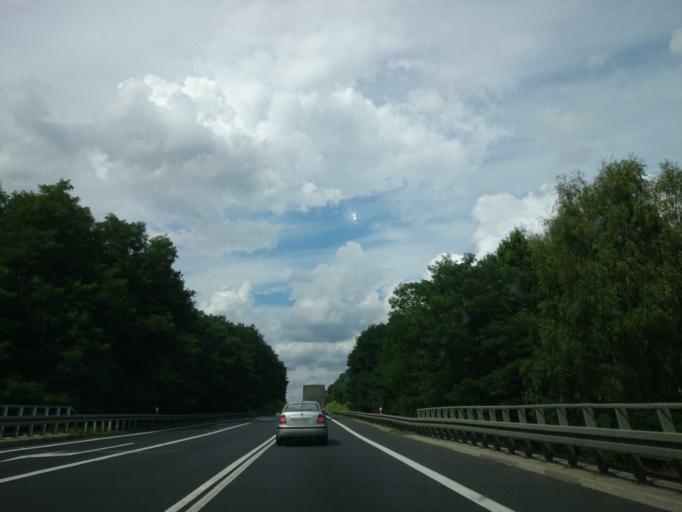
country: PL
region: Lubusz
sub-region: Zielona Gora
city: Zielona Gora
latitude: 51.9063
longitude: 15.5871
